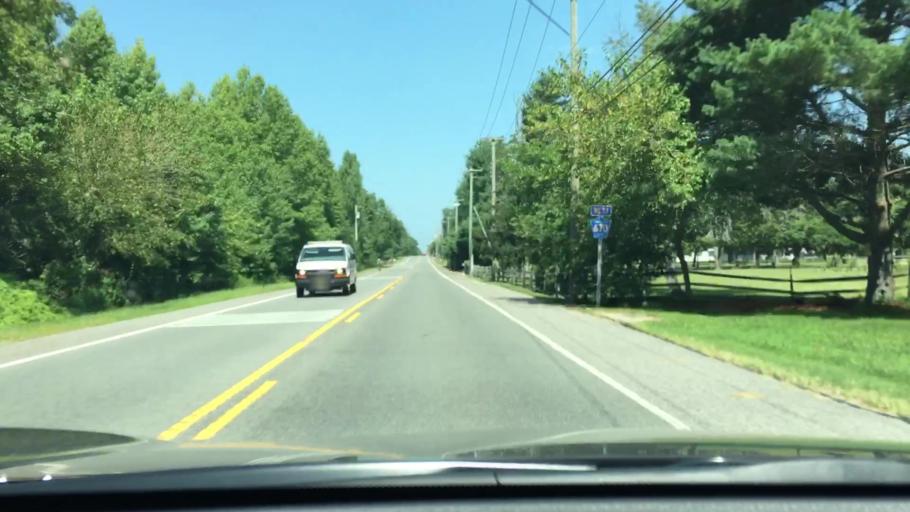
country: US
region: New Jersey
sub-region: Cumberland County
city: Port Norris
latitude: 39.2900
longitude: -74.9955
